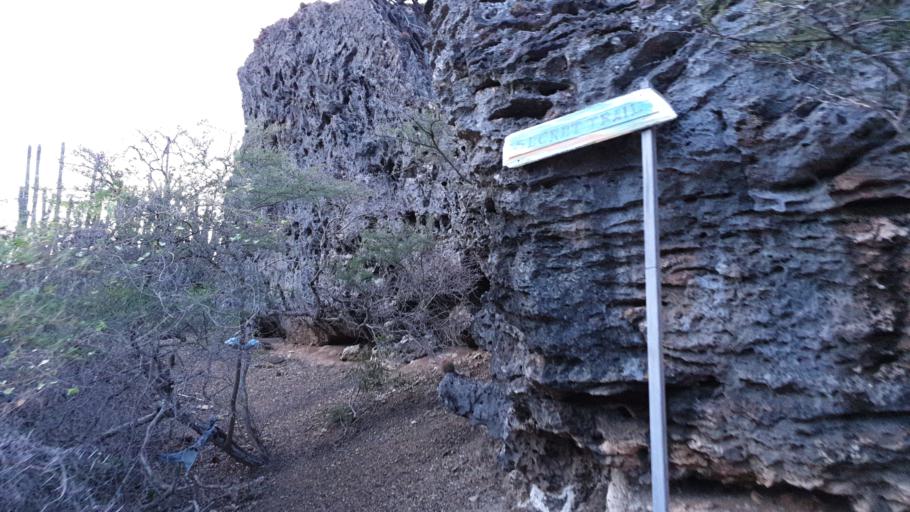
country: CW
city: Newport
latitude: 12.1333
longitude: -68.8158
